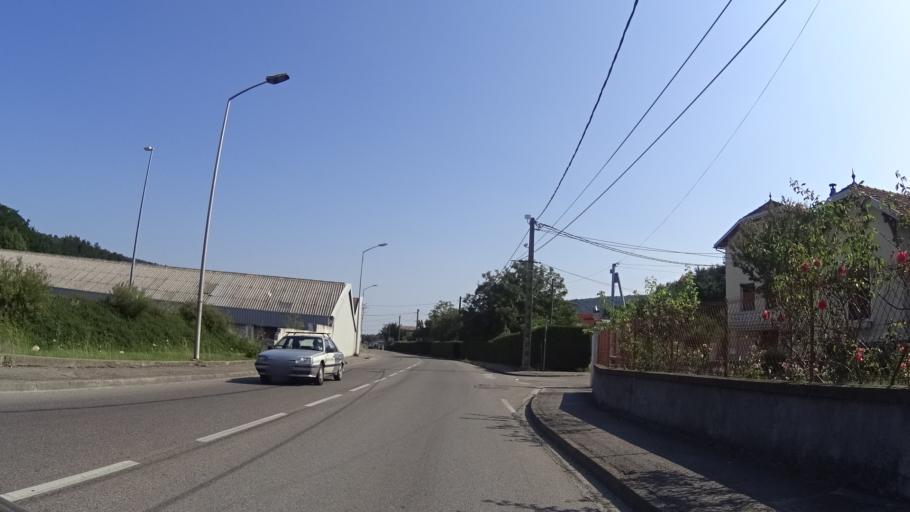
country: FR
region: Midi-Pyrenees
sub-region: Departement de l'Ariege
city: Lavelanet
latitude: 42.9426
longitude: 1.8565
